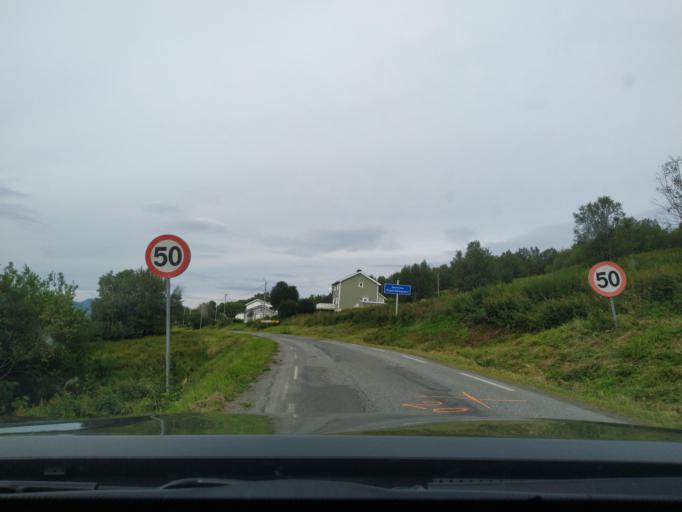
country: NO
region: Nordland
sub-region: Evenes
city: Randa
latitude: 68.7274
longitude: 16.8577
